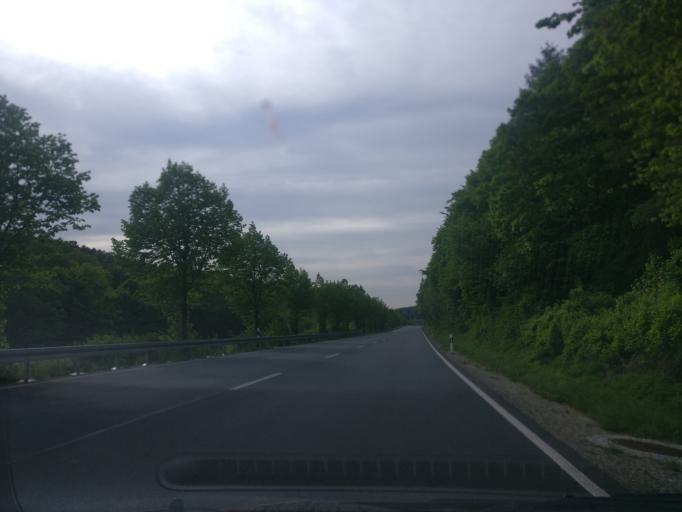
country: DE
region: Hesse
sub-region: Regierungsbezirk Kassel
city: Fuldatal
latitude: 51.3621
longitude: 9.5544
